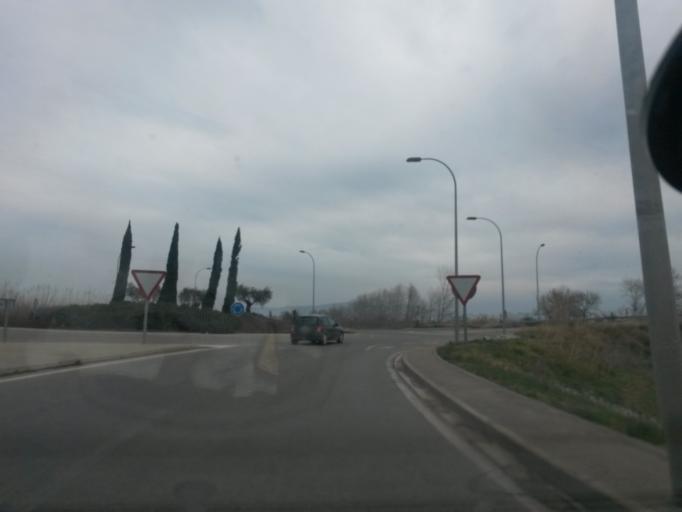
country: ES
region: Catalonia
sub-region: Provincia de Girona
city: Vilabertran
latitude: 42.2771
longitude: 2.9871
